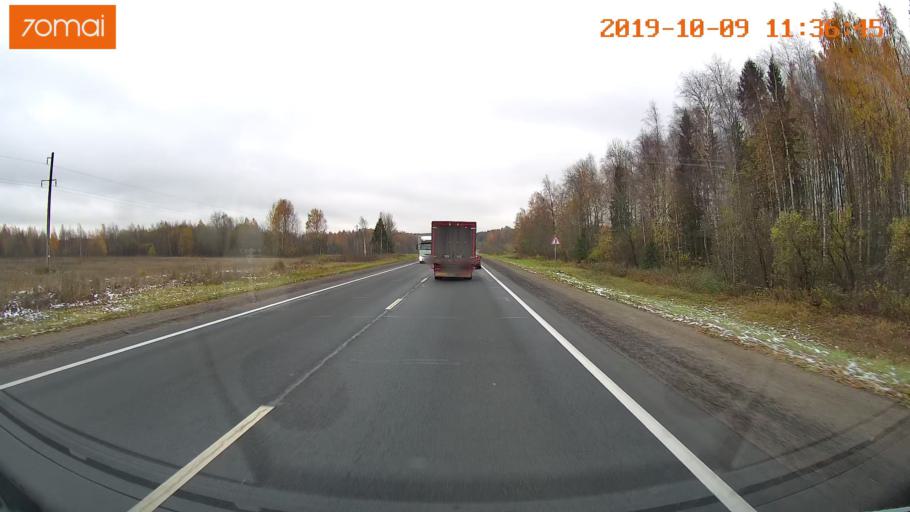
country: RU
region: Vologda
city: Gryazovets
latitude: 58.9863
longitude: 40.1407
